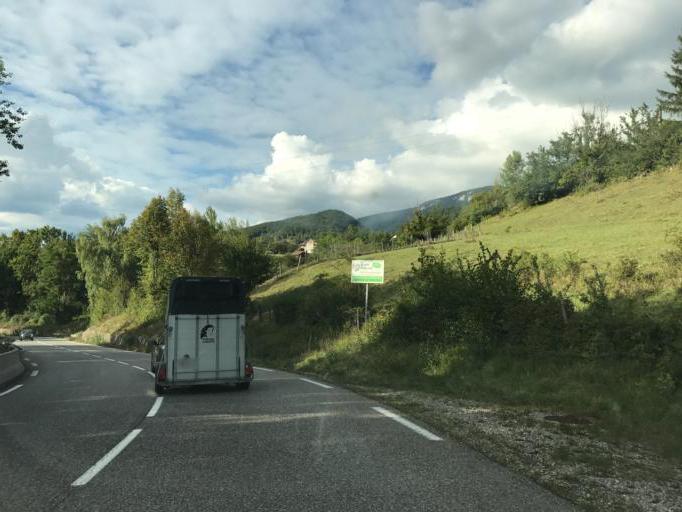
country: FR
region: Rhone-Alpes
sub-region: Departement de l'Ain
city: Bellegarde-sur-Valserine
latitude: 46.0997
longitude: 5.8449
